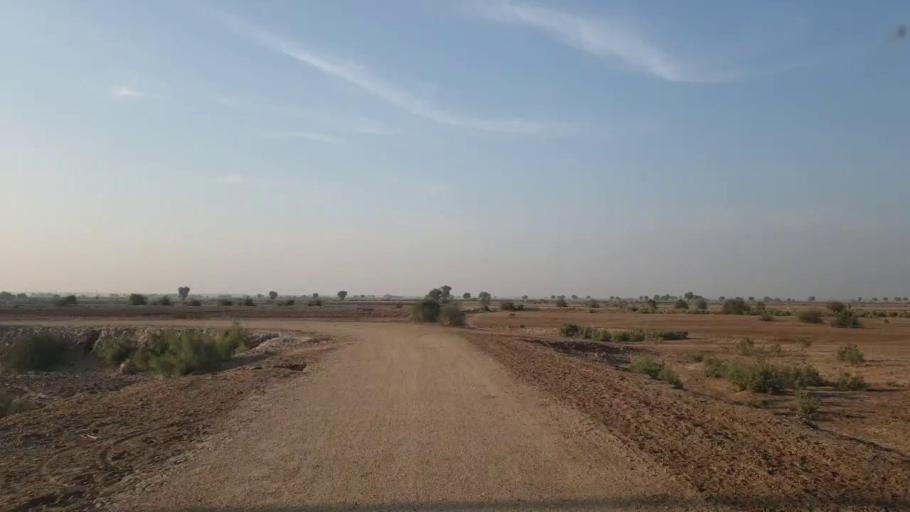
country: PK
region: Sindh
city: Sann
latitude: 25.9479
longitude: 68.1776
